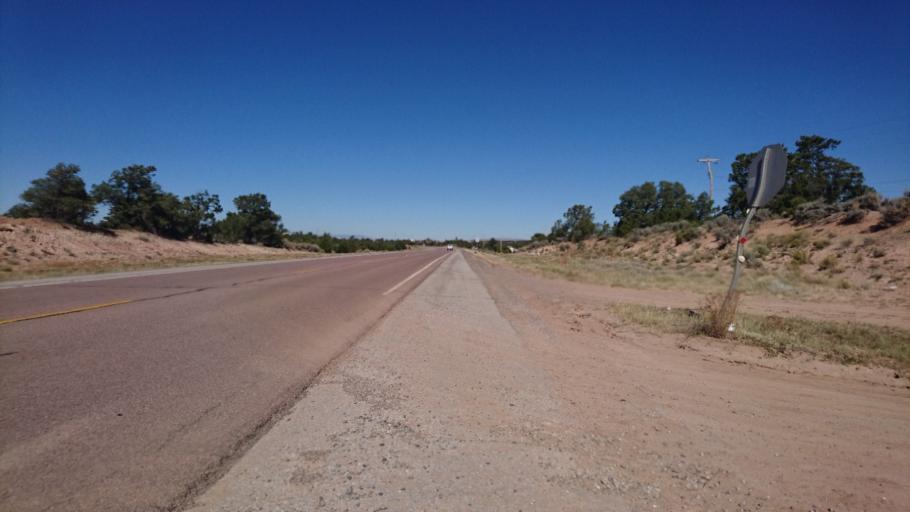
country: US
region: New Mexico
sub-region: McKinley County
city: Gallup
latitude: 35.3690
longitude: -108.7536
